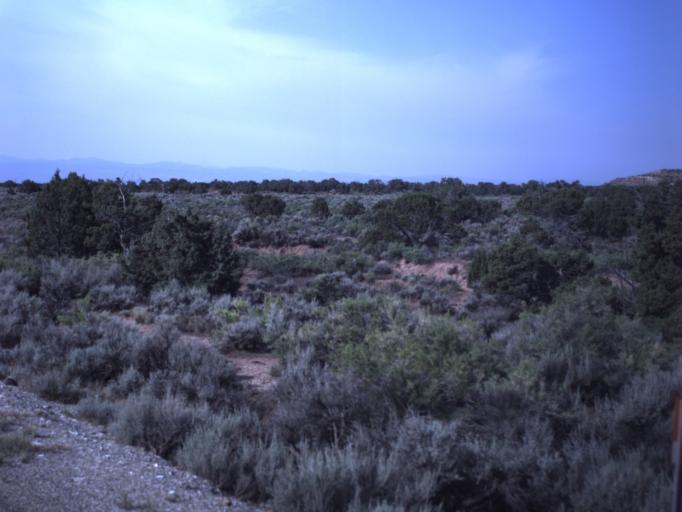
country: US
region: Utah
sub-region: Duchesne County
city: Duchesne
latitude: 40.2876
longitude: -110.3766
